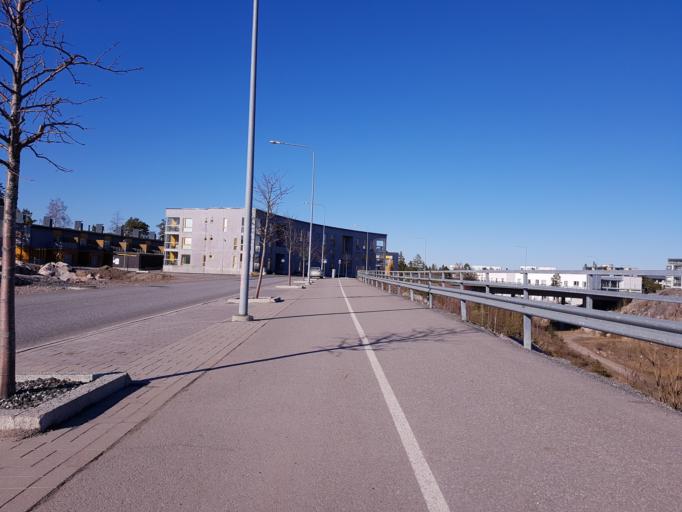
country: FI
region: Uusimaa
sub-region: Helsinki
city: Helsinki
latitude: 60.2282
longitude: 24.9901
